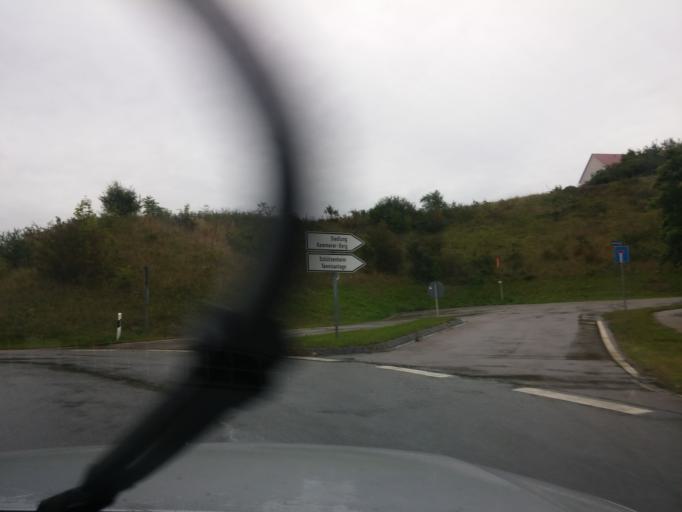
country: DE
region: Bavaria
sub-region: Upper Bavaria
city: Reichertshausen
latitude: 48.4636
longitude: 11.5106
